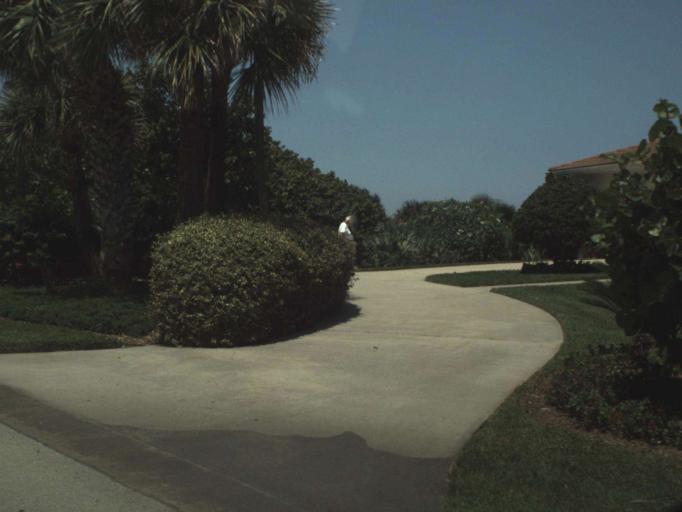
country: US
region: Florida
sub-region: Brevard County
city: Malabar
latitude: 28.0288
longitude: -80.5391
